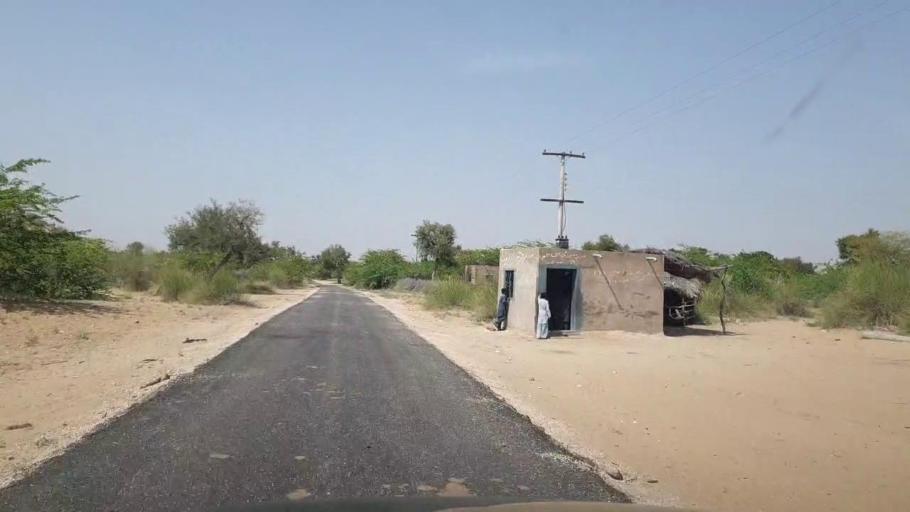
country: PK
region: Sindh
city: Islamkot
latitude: 25.1081
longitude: 70.6526
